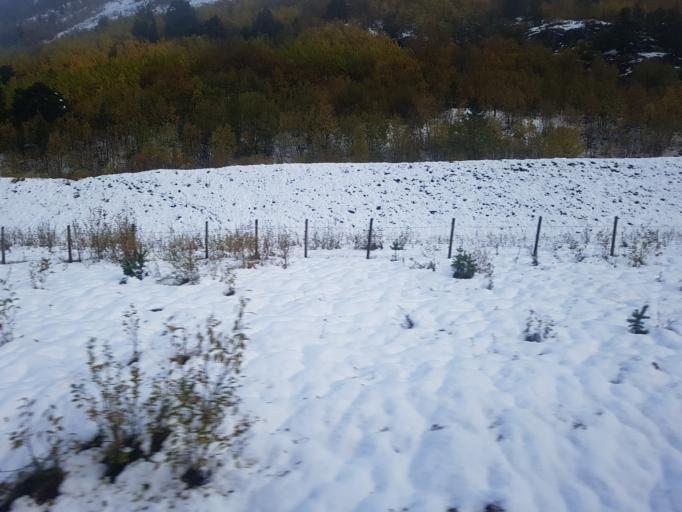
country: NO
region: Sor-Trondelag
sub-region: Oppdal
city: Oppdal
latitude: 62.4290
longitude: 9.6108
